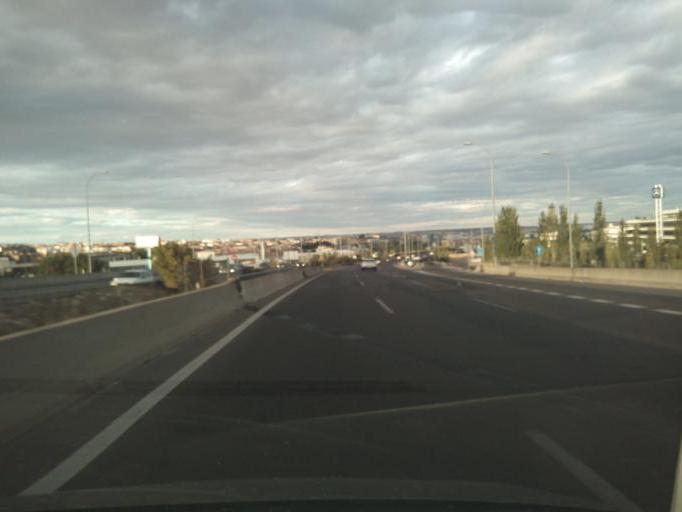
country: ES
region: Madrid
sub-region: Provincia de Madrid
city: Alcobendas
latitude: 40.5306
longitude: -3.6440
